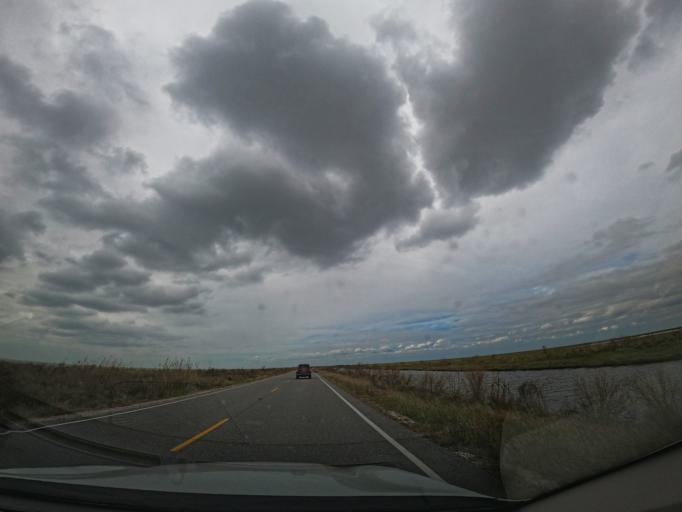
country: US
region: Louisiana
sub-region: Cameron Parish
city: Cameron
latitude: 29.7672
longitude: -93.3872
